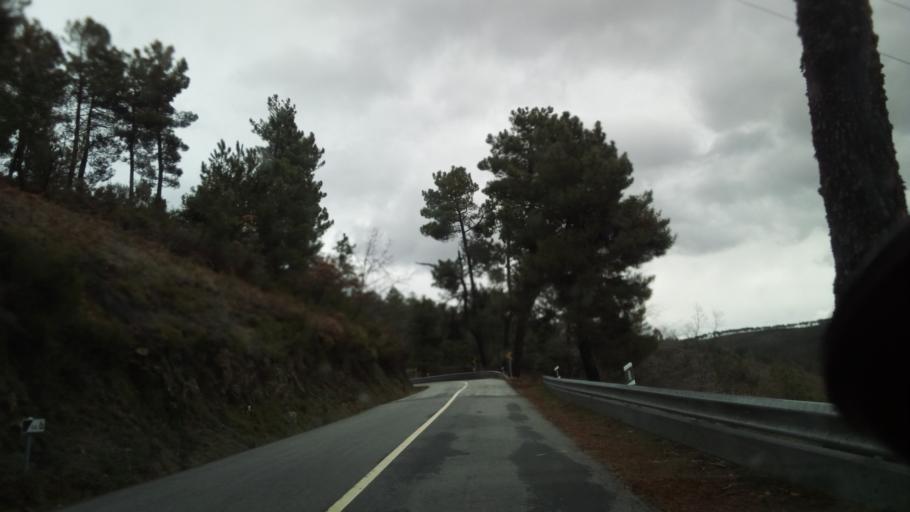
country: PT
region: Guarda
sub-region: Manteigas
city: Manteigas
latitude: 40.4151
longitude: -7.5334
